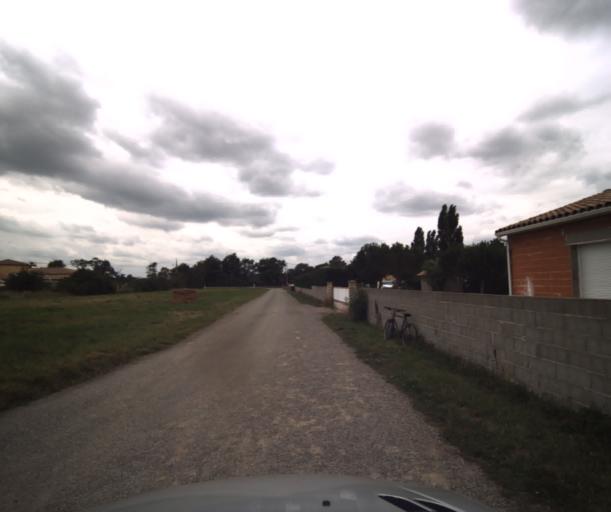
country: FR
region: Midi-Pyrenees
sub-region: Departement de la Haute-Garonne
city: Labarthe-sur-Leze
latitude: 43.4515
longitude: 1.4176
